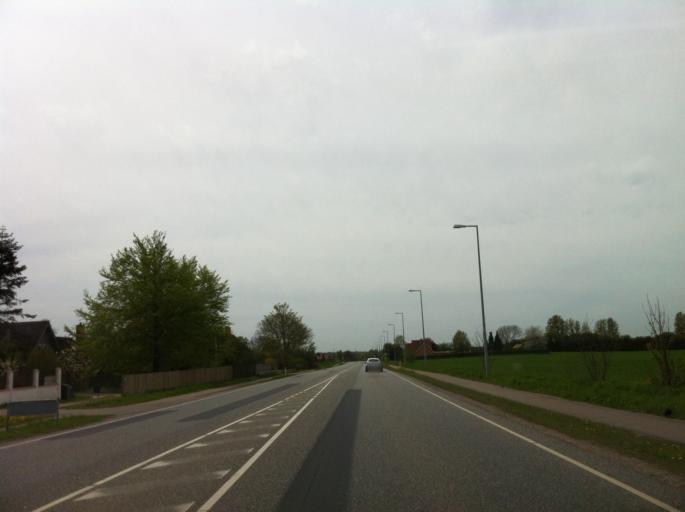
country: DK
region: Zealand
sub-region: Ringsted Kommune
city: Ringsted
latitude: 55.4842
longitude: 11.8485
